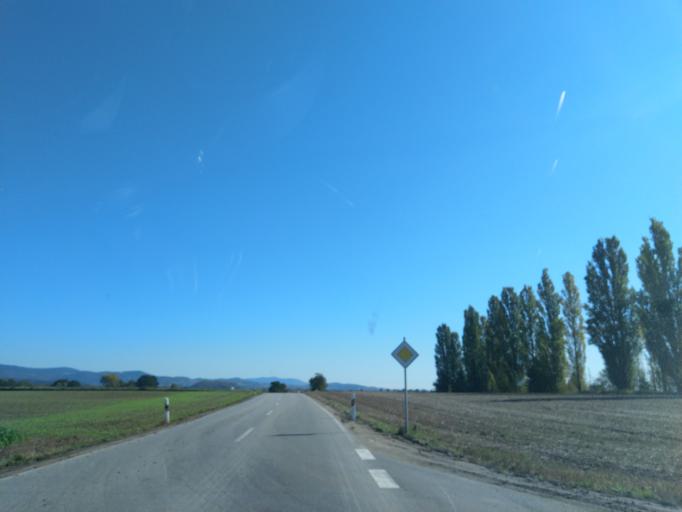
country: DE
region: Bavaria
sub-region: Lower Bavaria
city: Offenberg
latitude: 48.8219
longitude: 12.8546
